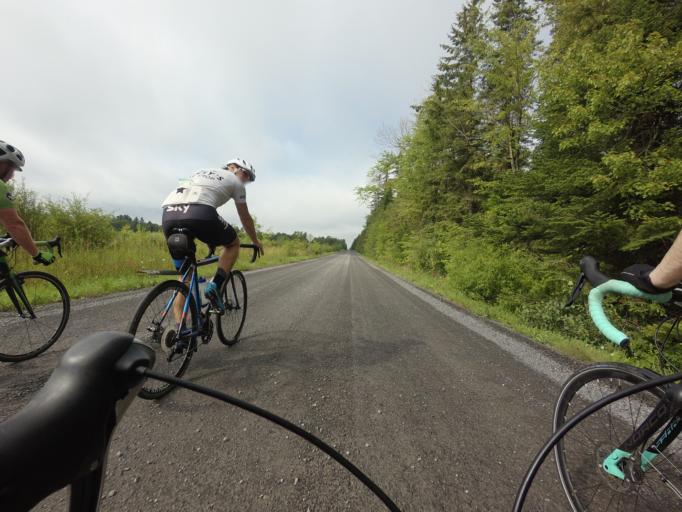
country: CA
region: Ontario
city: Bells Corners
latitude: 45.0558
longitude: -75.7168
